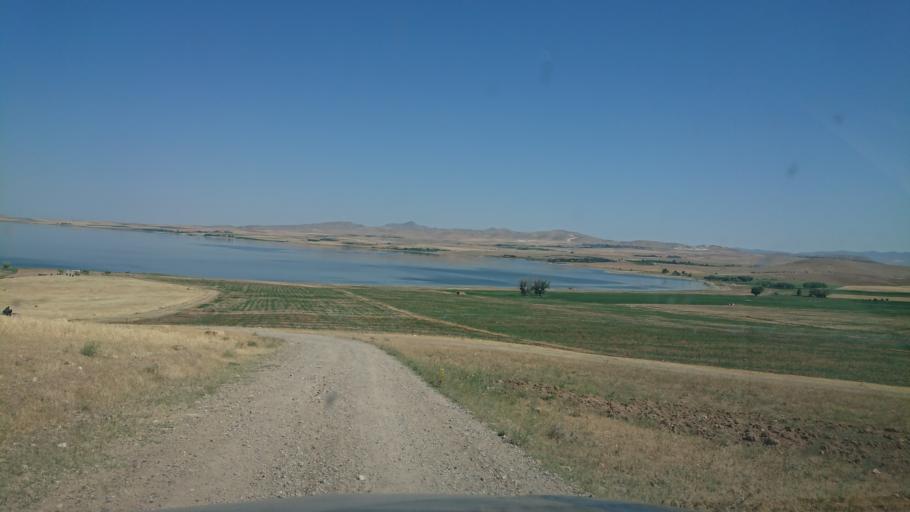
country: TR
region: Aksaray
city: Sariyahsi
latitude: 39.0555
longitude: 33.8843
